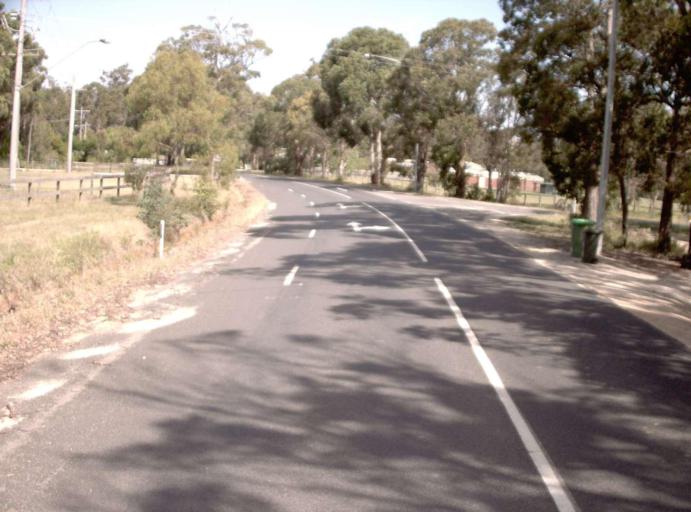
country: AU
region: New South Wales
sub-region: Bega Valley
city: Eden
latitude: -37.5532
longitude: 149.7403
